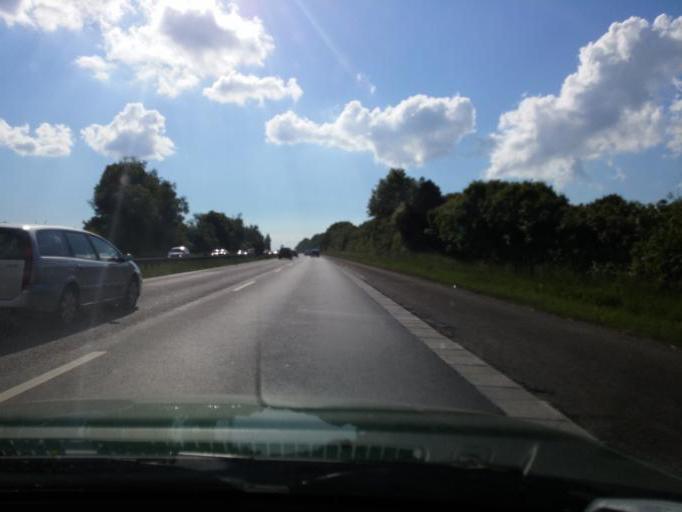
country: DK
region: South Denmark
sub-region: Assens Kommune
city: Vissenbjerg
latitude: 55.4109
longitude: 10.0996
